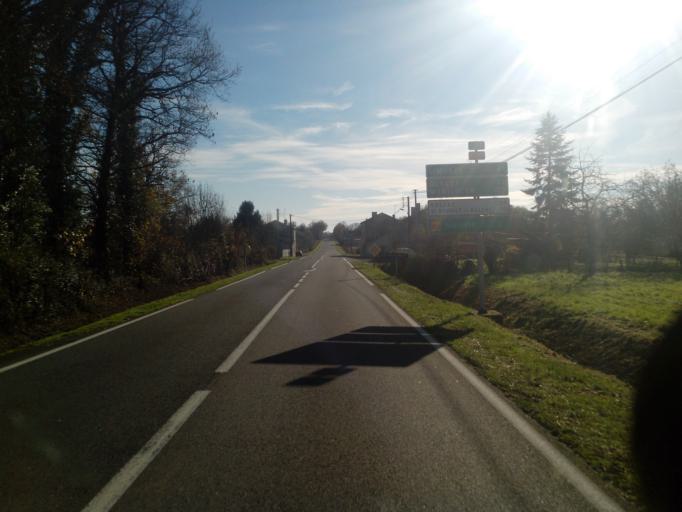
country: FR
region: Limousin
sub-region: Departement de la Haute-Vienne
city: Bussiere-Poitevine
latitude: 46.2384
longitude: 0.8939
